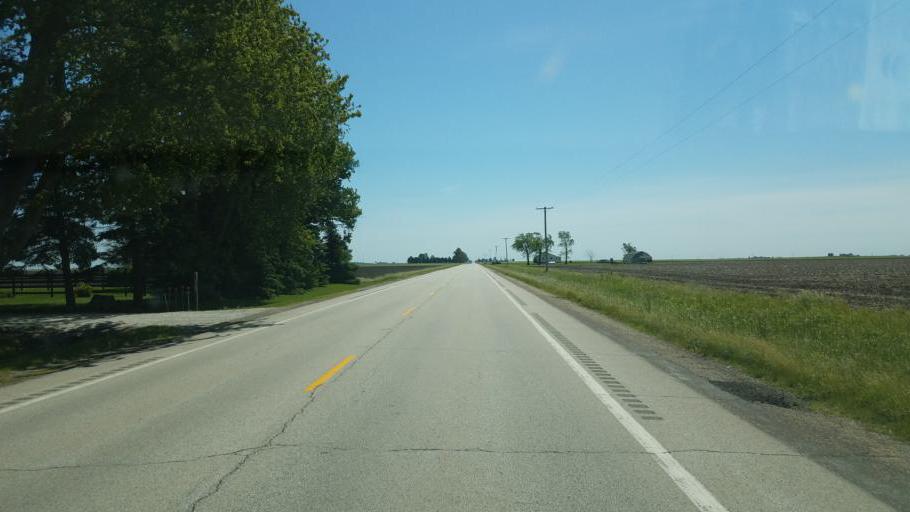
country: US
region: Illinois
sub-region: McLean County
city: Downs
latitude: 40.3122
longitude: -88.8766
